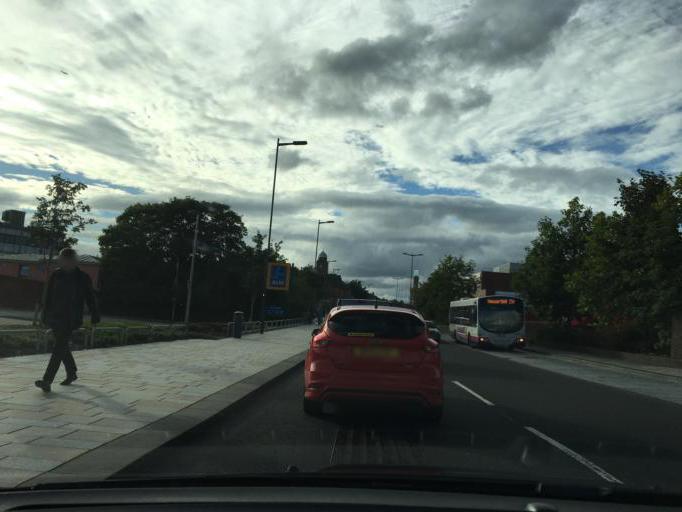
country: GB
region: Scotland
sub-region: North Lanarkshire
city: Motherwell
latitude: 55.7883
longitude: -3.9908
